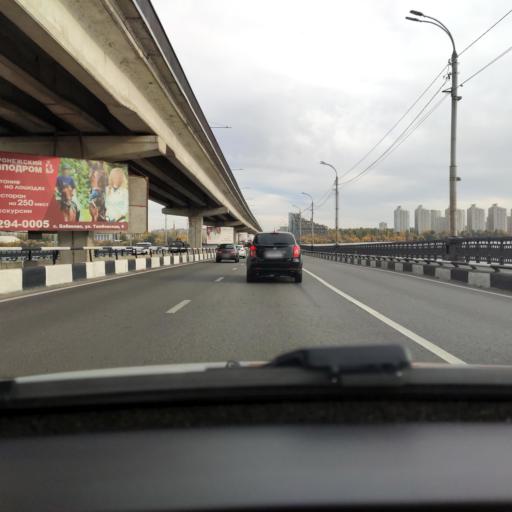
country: RU
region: Voronezj
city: Voronezh
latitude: 51.6934
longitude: 39.2374
